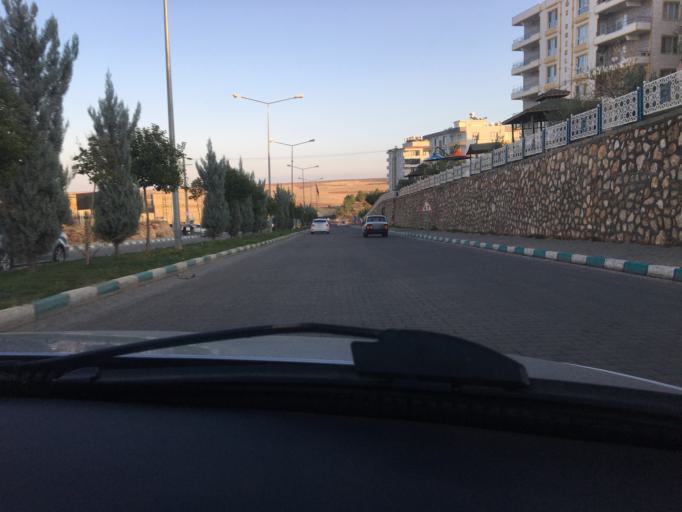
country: TR
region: Sanliurfa
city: Halfeti
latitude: 37.2302
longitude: 37.9483
